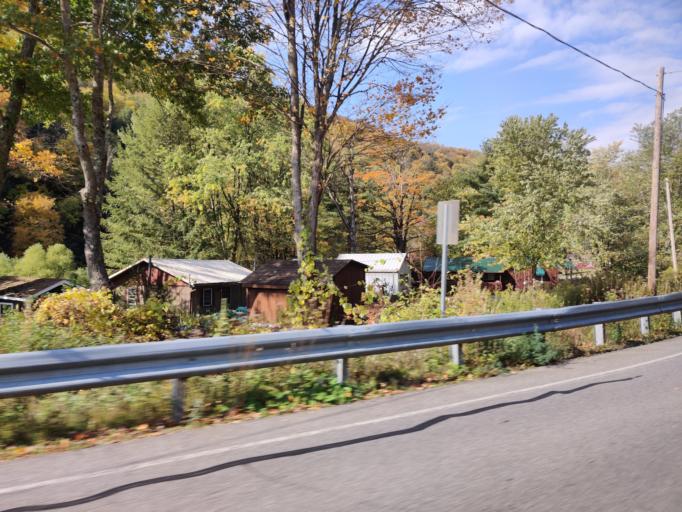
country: US
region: Pennsylvania
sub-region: Warren County
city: Sheffield
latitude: 41.6374
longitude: -79.0441
